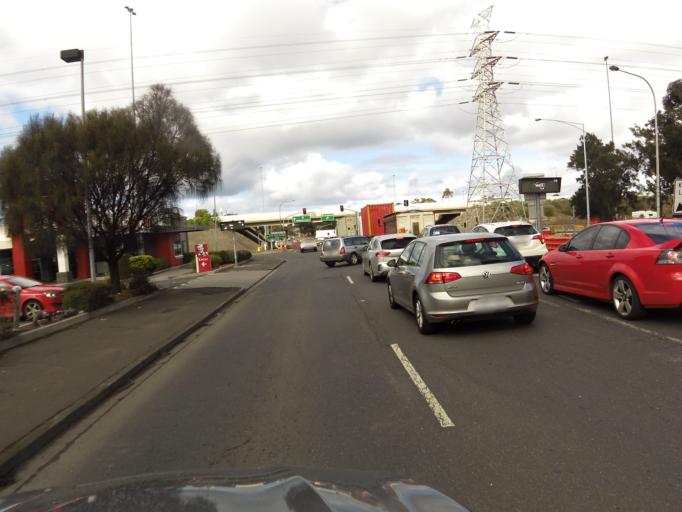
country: AU
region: Victoria
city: Spotswood
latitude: -37.8241
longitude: 144.8813
